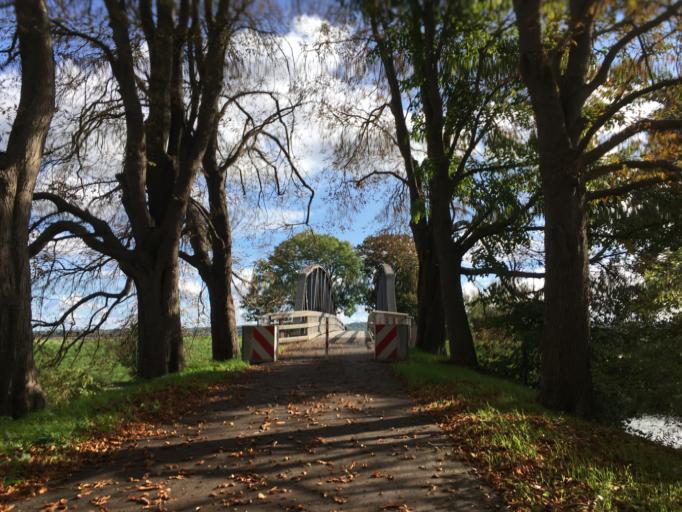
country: DE
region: Brandenburg
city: Meyenburg
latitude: 53.0367
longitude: 14.2578
